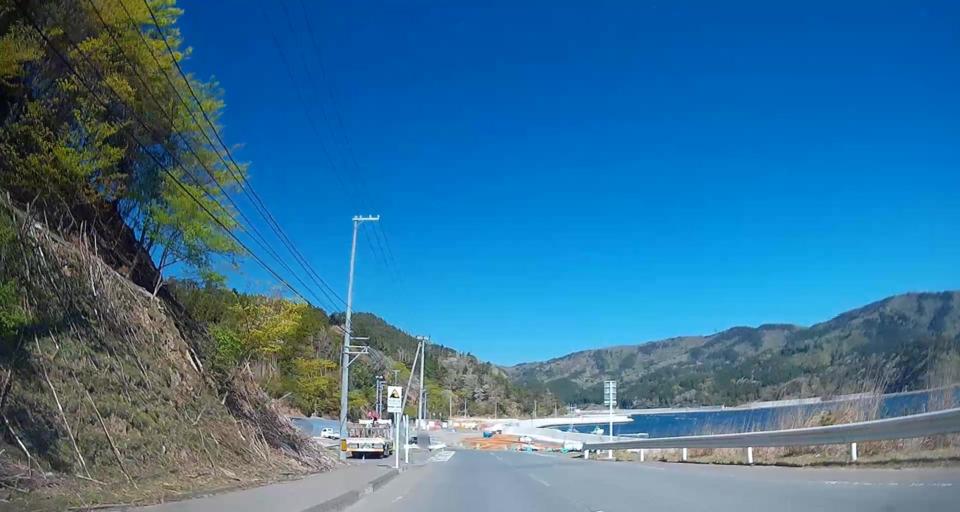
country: JP
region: Miyagi
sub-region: Oshika Gun
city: Onagawa Cho
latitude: 38.5125
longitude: 141.4802
